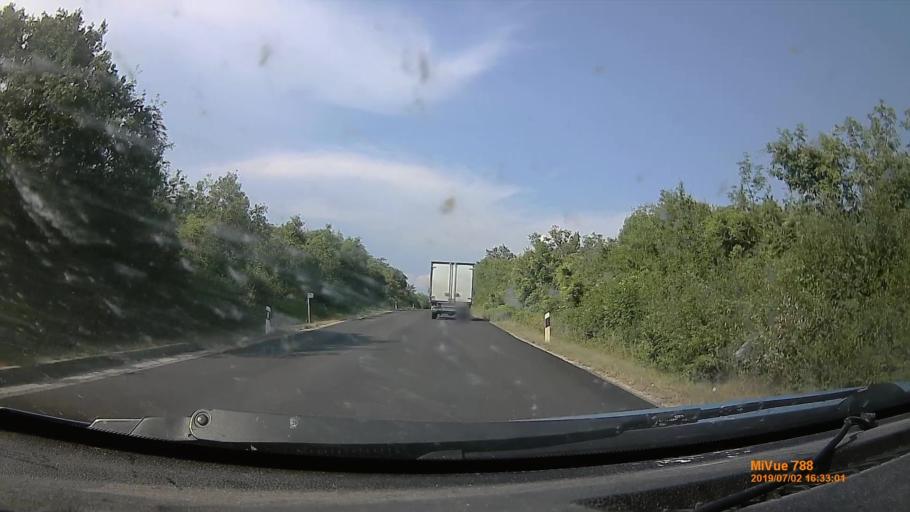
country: HR
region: Primorsko-Goranska
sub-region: Grad Krk
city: Krk
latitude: 45.0705
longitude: 14.4883
